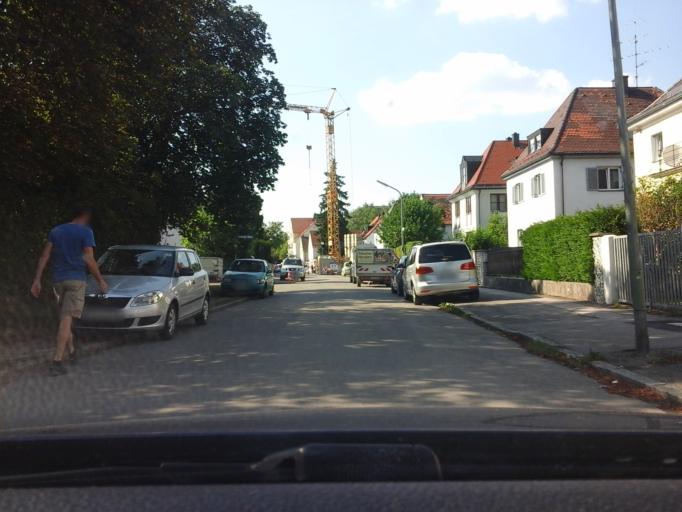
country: DE
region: Bavaria
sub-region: Upper Bavaria
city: Munich
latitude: 48.0966
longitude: 11.5835
